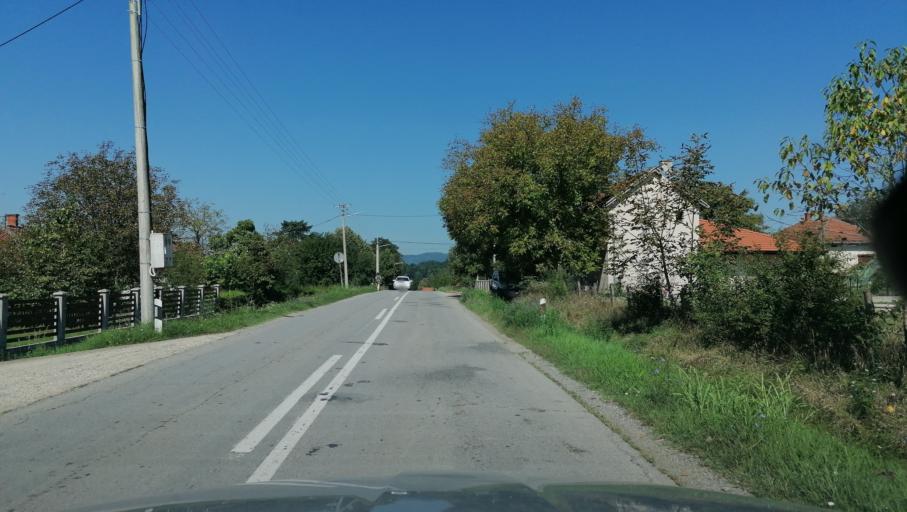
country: RS
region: Central Serbia
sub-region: Raski Okrug
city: Vrnjacka Banja
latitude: 43.7109
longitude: 20.8346
